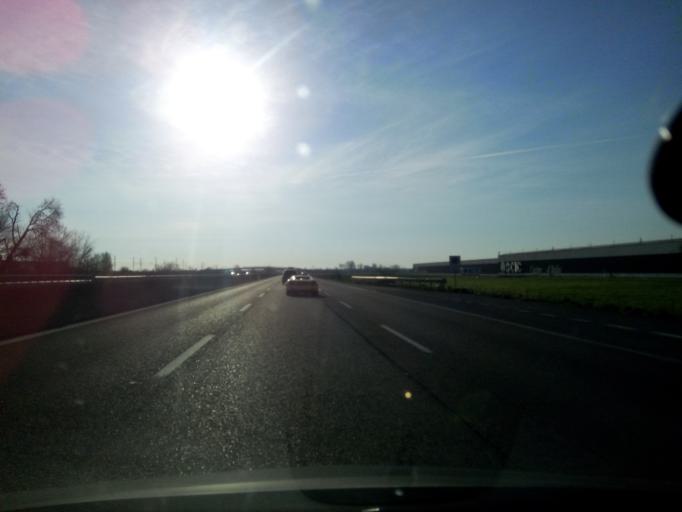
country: IT
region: Emilia-Romagna
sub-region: Provincia di Parma
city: Baganzola
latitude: 44.8587
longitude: 10.2604
